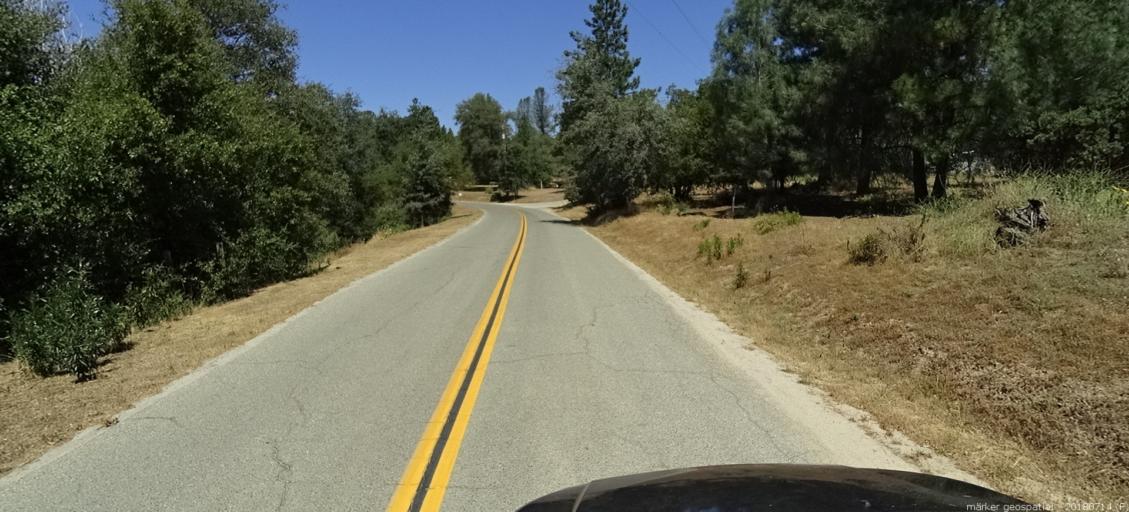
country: US
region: California
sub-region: Madera County
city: Ahwahnee
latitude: 37.3848
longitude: -119.6762
